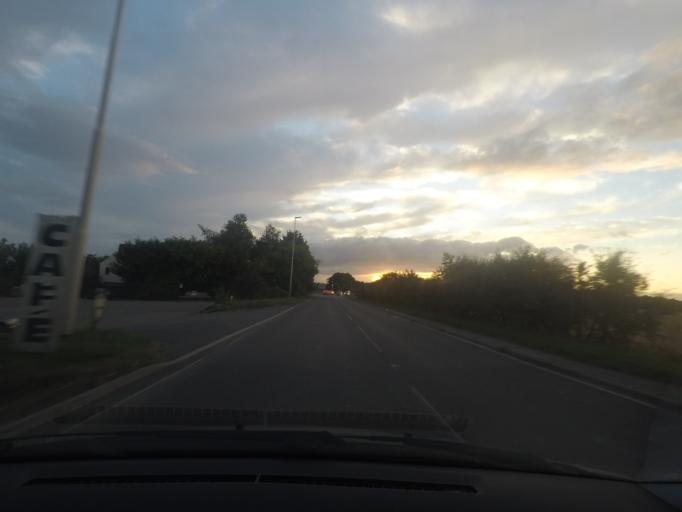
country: GB
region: England
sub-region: North Lincolnshire
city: Barnetby le Wold
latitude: 53.5823
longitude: -0.4070
